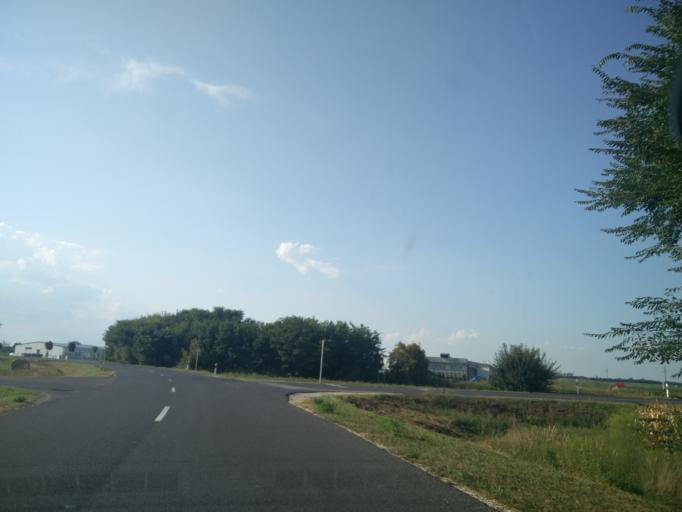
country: HU
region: Zala
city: Zalaegerszeg
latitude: 46.8789
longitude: 16.8303
